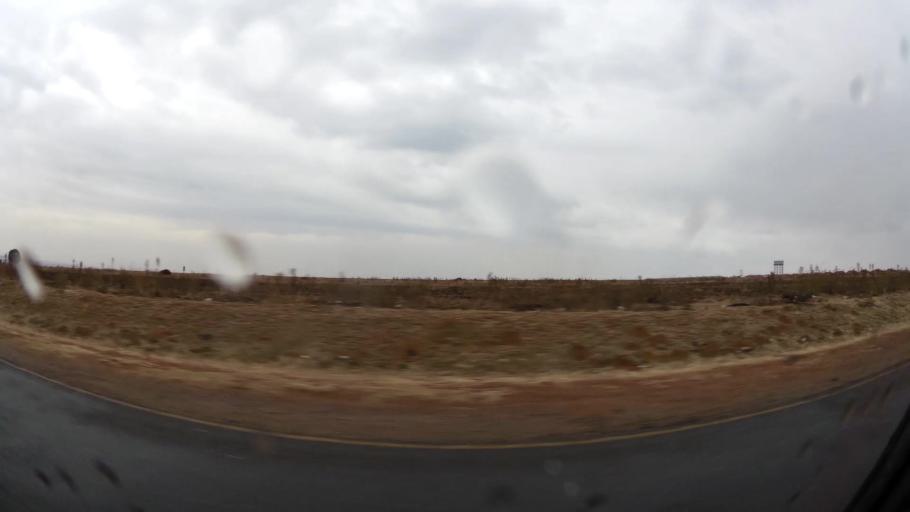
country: ZA
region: Gauteng
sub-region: City of Johannesburg Metropolitan Municipality
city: Roodepoort
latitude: -26.1738
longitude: 27.8033
